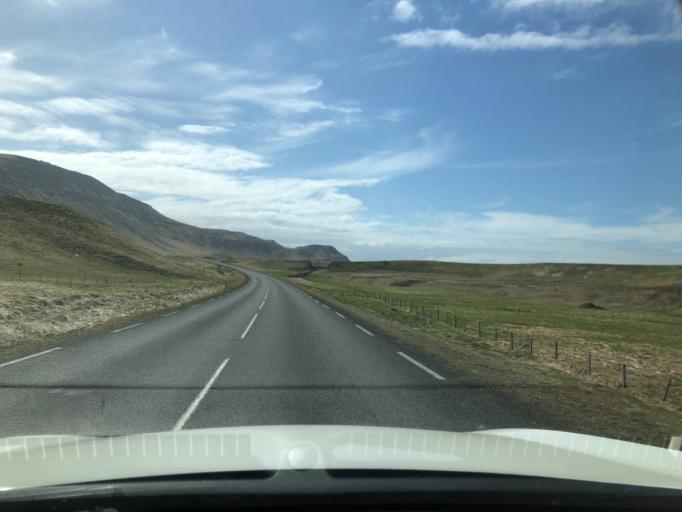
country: IS
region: Capital Region
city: Mosfellsbaer
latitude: 64.3045
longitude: -21.7846
